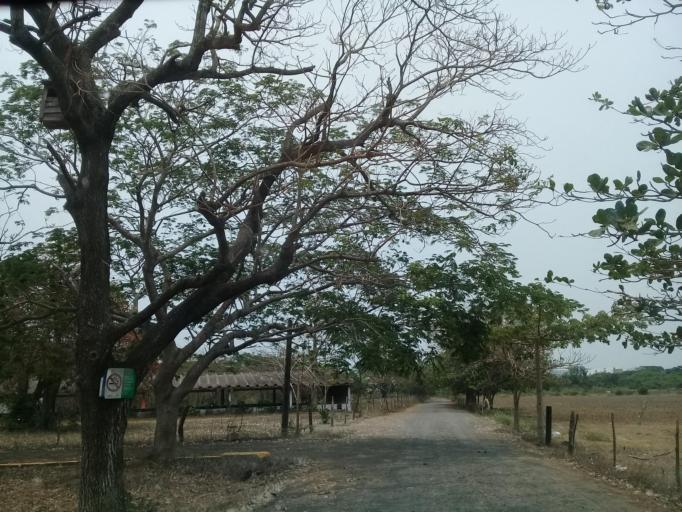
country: MX
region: Veracruz
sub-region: Veracruz
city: Lomas de Rio Medio Cuatro
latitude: 19.1734
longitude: -96.2102
